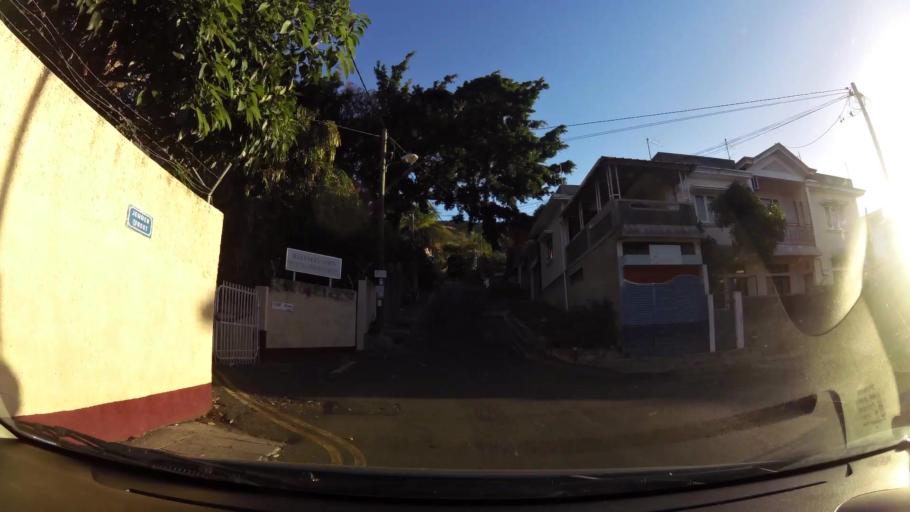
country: MU
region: Port Louis
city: Port Louis
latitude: -20.1750
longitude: 57.5051
